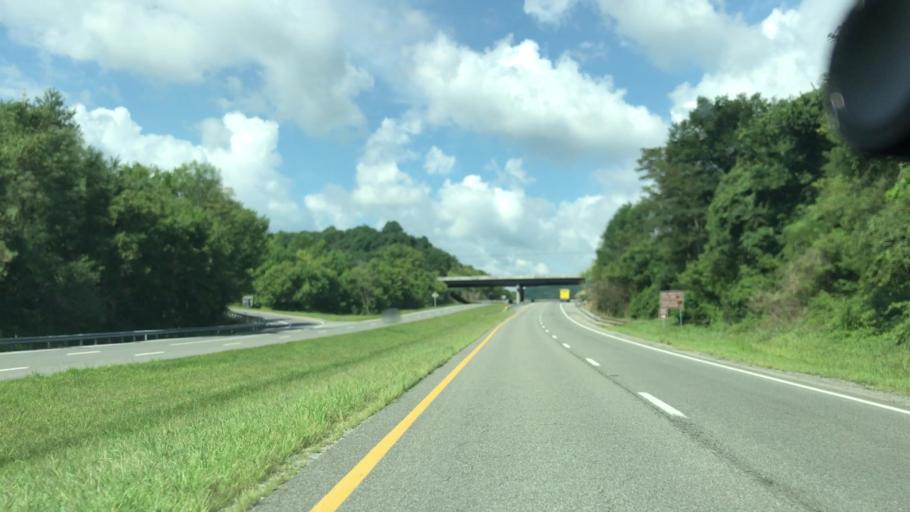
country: US
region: Virginia
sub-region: Giles County
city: Pearisburg
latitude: 37.3365
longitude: -80.7354
